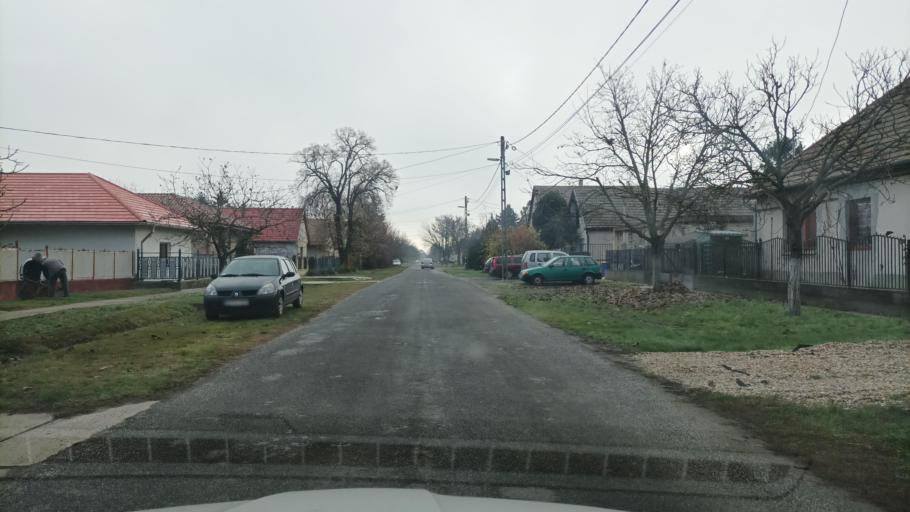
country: HU
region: Pest
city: Szigetcsep
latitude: 47.2686
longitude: 18.9584
